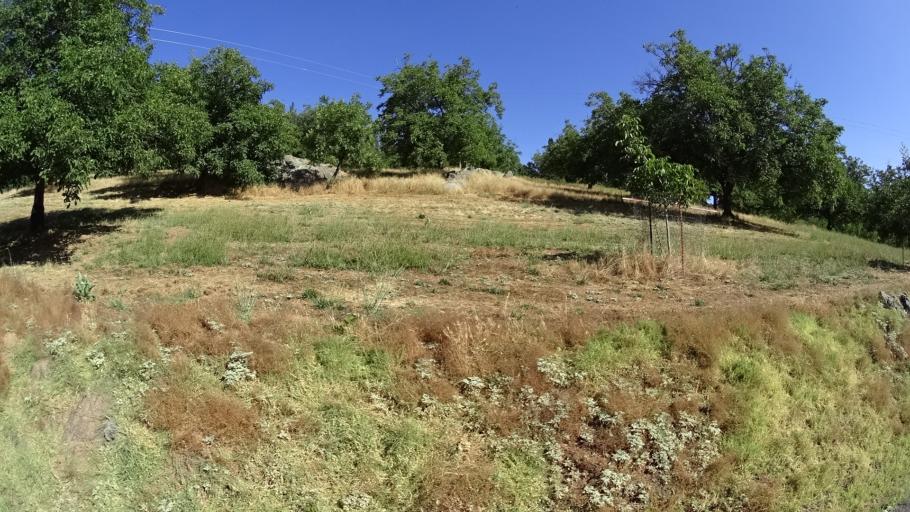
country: US
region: California
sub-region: Amador County
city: Pioneer
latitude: 38.3985
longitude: -120.5607
